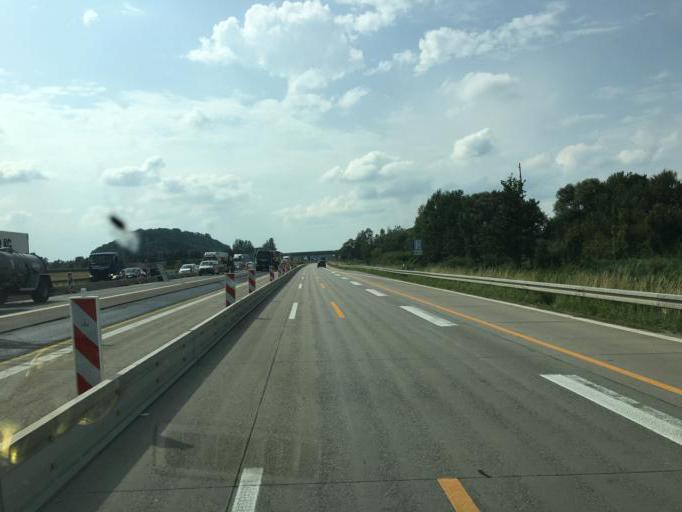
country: DE
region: Bavaria
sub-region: Lower Bavaria
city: Deggendorf
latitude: 48.8214
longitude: 12.9315
